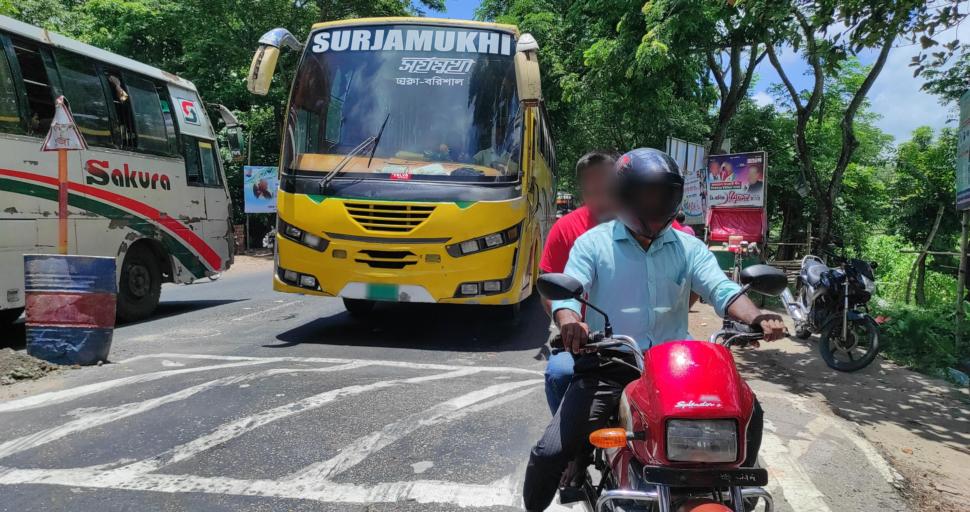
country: BD
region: Barisal
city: Gaurnadi
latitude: 22.8305
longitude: 90.2573
